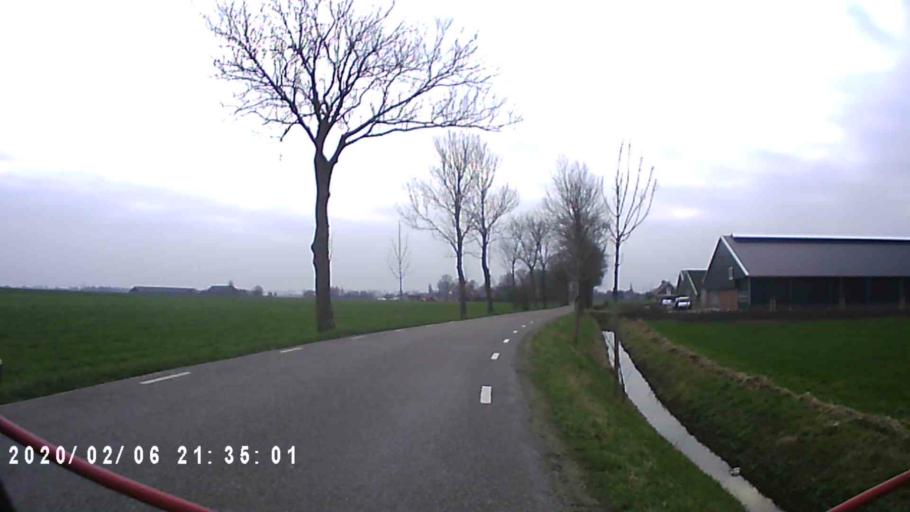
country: NL
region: Groningen
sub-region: Gemeente Zuidhorn
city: Noordhorn
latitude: 53.2716
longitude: 6.3912
